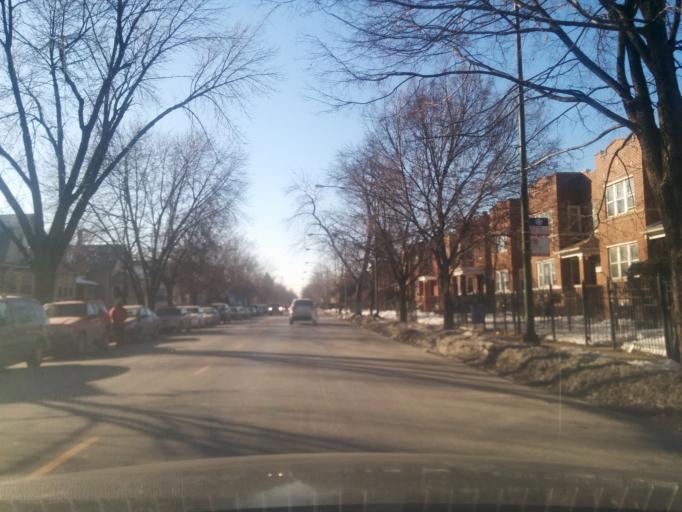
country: US
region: Illinois
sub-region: Cook County
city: Elmwood Park
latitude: 41.9272
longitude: -87.7759
